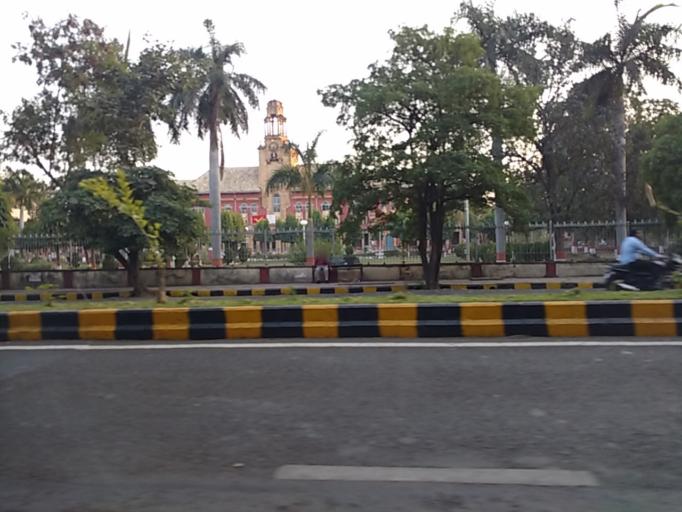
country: IN
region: Maharashtra
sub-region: Nagpur Division
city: Nagpur
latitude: 21.1535
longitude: 79.0692
